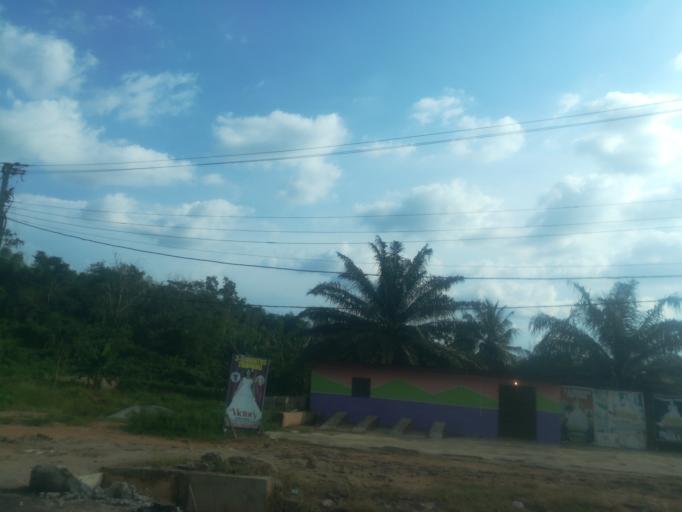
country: NG
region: Oyo
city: Ibadan
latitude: 7.4156
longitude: 3.8520
